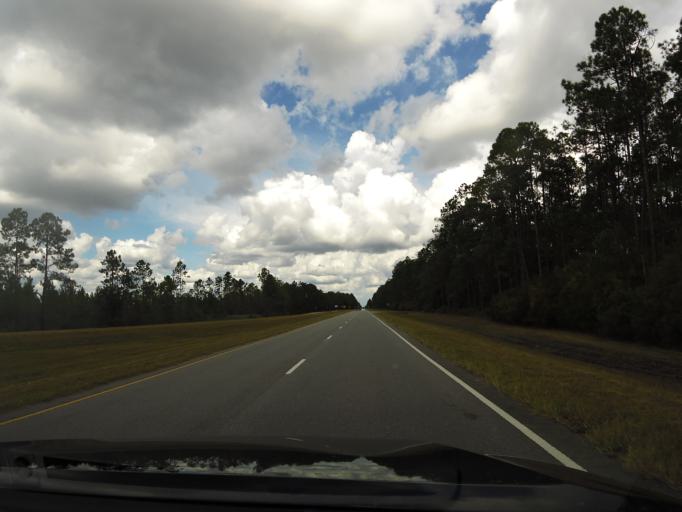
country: US
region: Georgia
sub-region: Charlton County
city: Folkston
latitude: 30.8782
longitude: -82.0138
